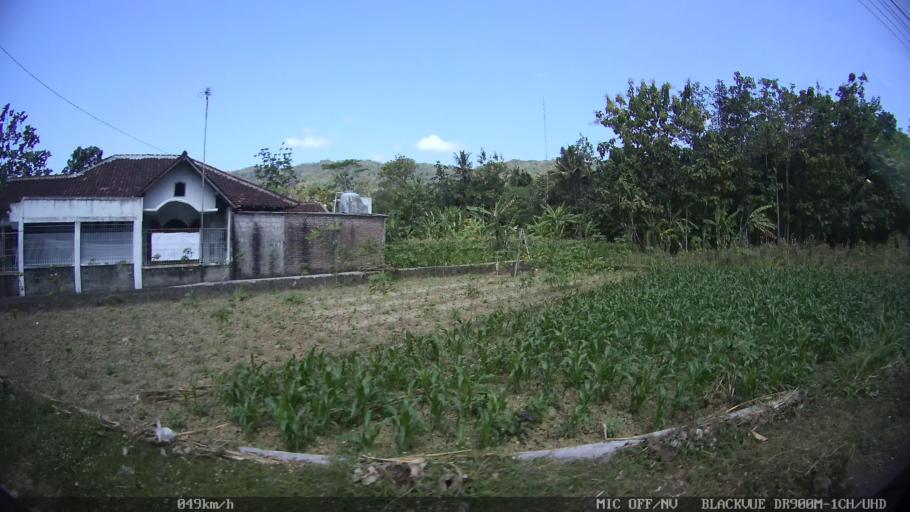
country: ID
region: Daerah Istimewa Yogyakarta
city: Pundong
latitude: -7.9828
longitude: 110.3353
